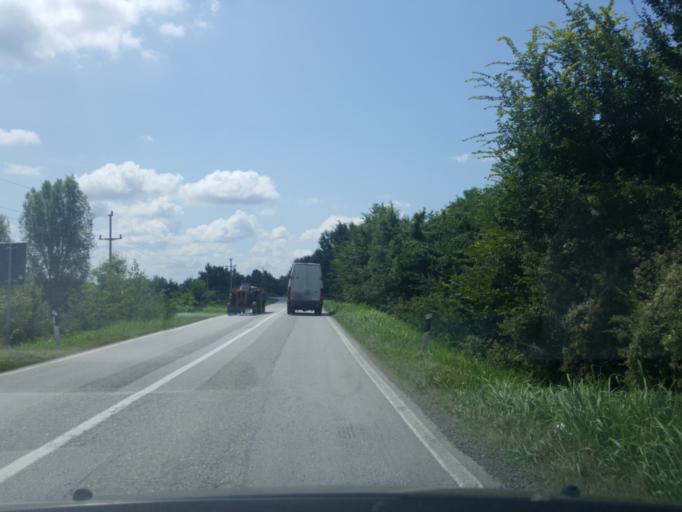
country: RS
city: Glusci
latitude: 44.9230
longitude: 19.5439
